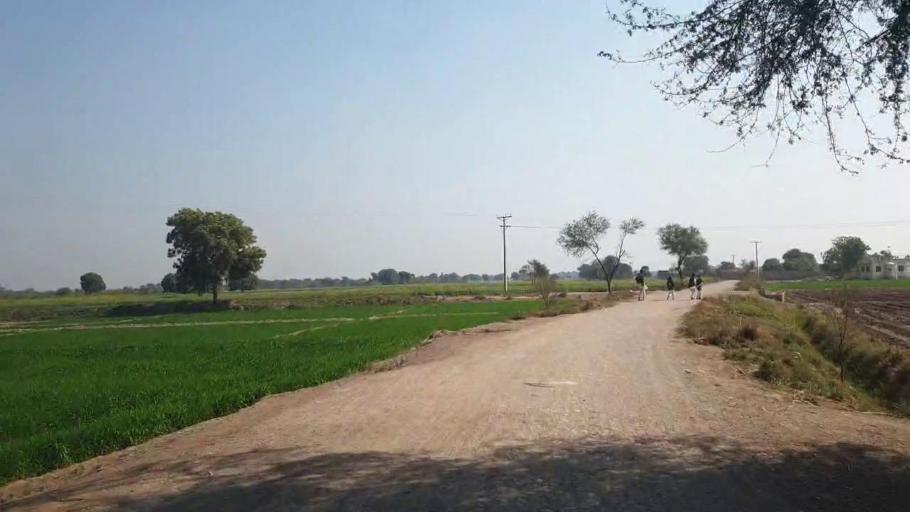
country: PK
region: Sindh
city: Tando Jam
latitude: 25.3279
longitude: 68.6351
